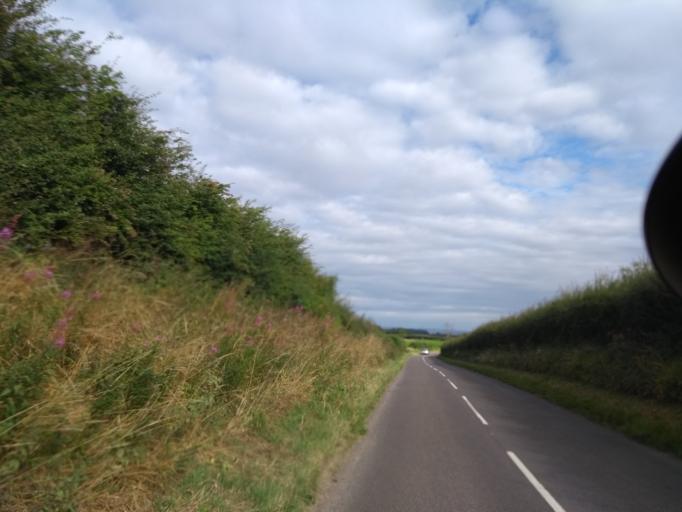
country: GB
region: England
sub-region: Somerset
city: Ilminster
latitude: 50.9153
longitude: -2.8769
